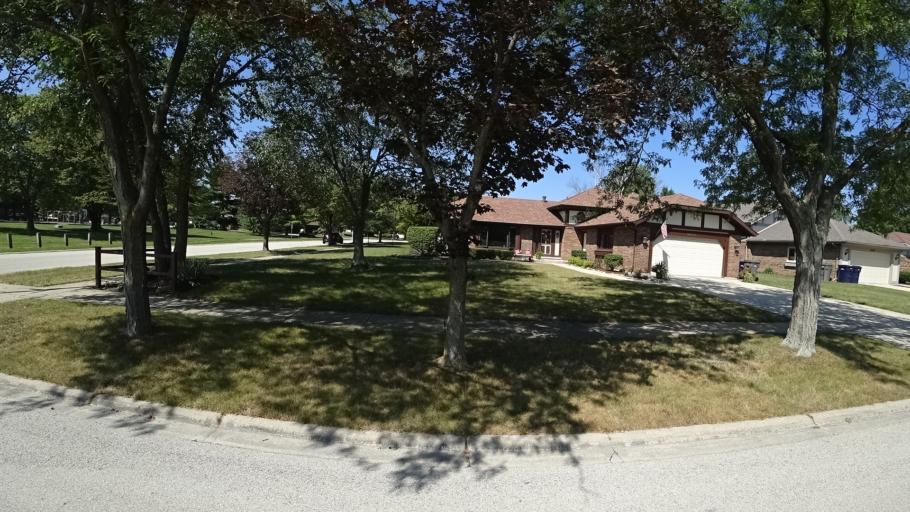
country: US
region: Illinois
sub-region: Cook County
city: Orland Park
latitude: 41.6347
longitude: -87.8230
